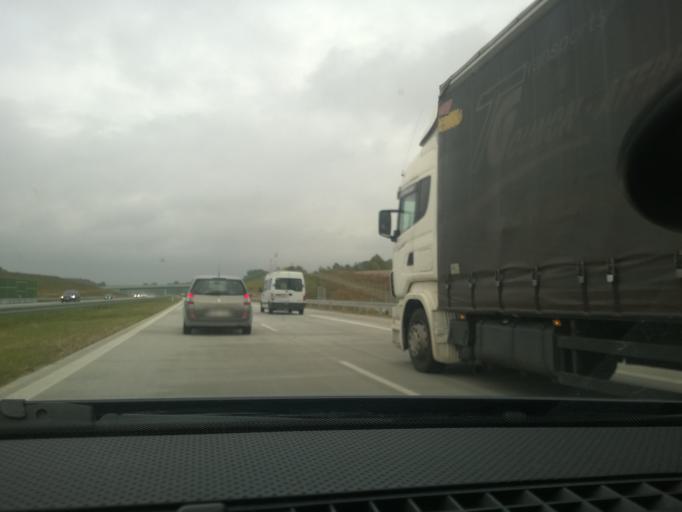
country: PL
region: Lodz Voivodeship
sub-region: Powiat lodzki wschodni
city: Andrespol
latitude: 51.8188
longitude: 19.6442
